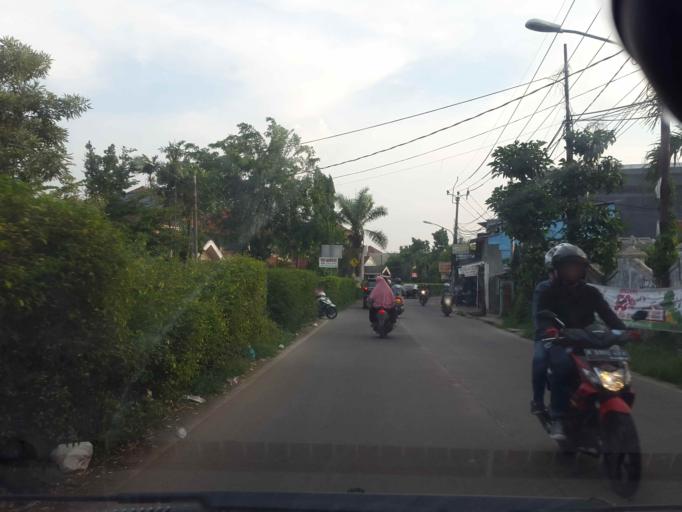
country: ID
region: Banten
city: South Tangerang
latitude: -6.2646
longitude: 106.7445
